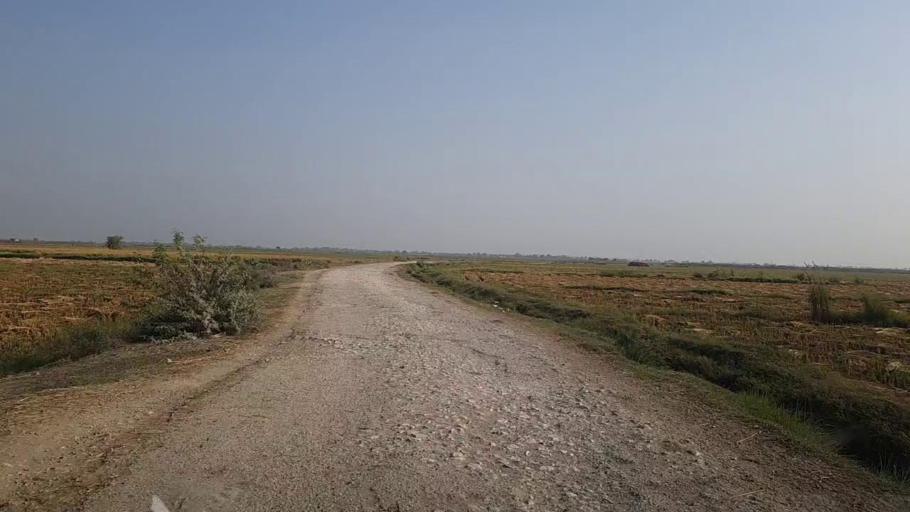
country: PK
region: Sindh
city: Kandhkot
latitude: 28.3008
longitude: 69.2506
